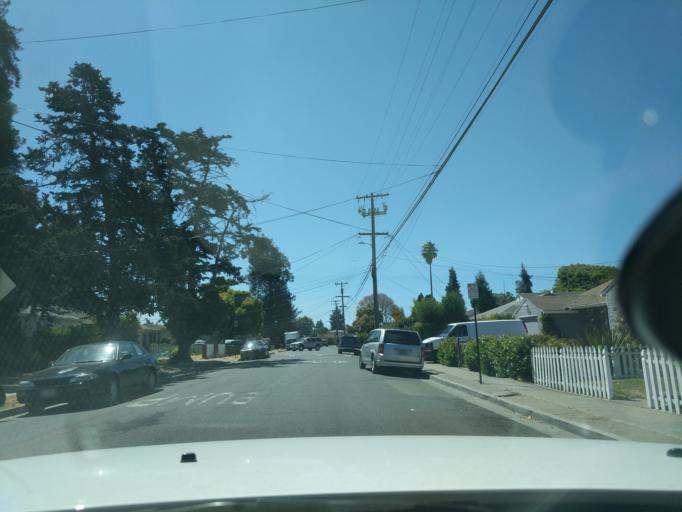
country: US
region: California
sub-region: Alameda County
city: Hayward
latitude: 37.6655
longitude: -122.0913
